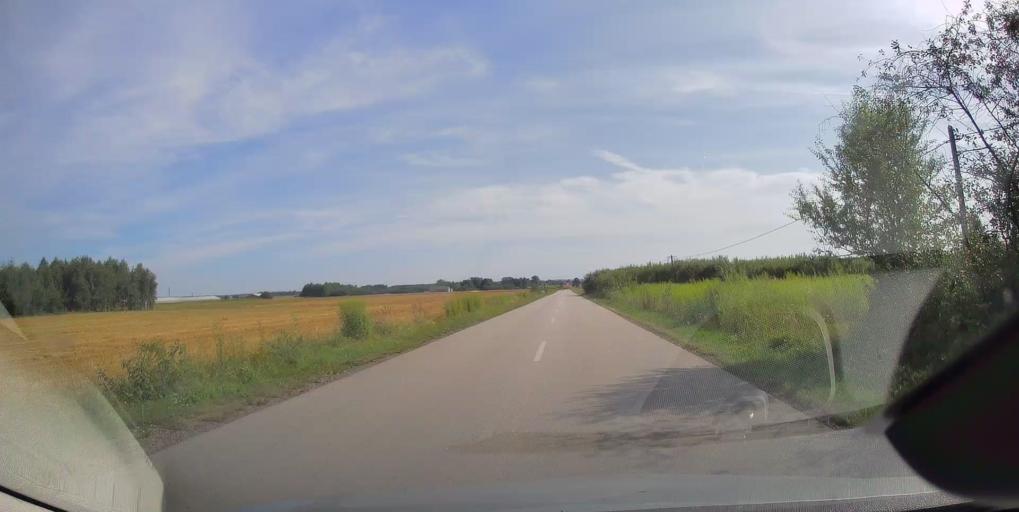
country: PL
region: Lodz Voivodeship
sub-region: Powiat opoczynski
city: Mniszkow
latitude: 51.3647
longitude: 20.0381
